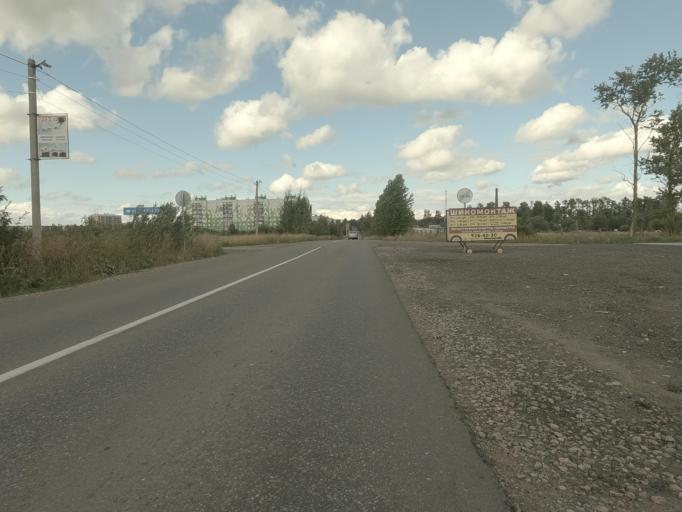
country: RU
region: Leningrad
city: Shcheglovo
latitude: 60.0218
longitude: 30.7475
